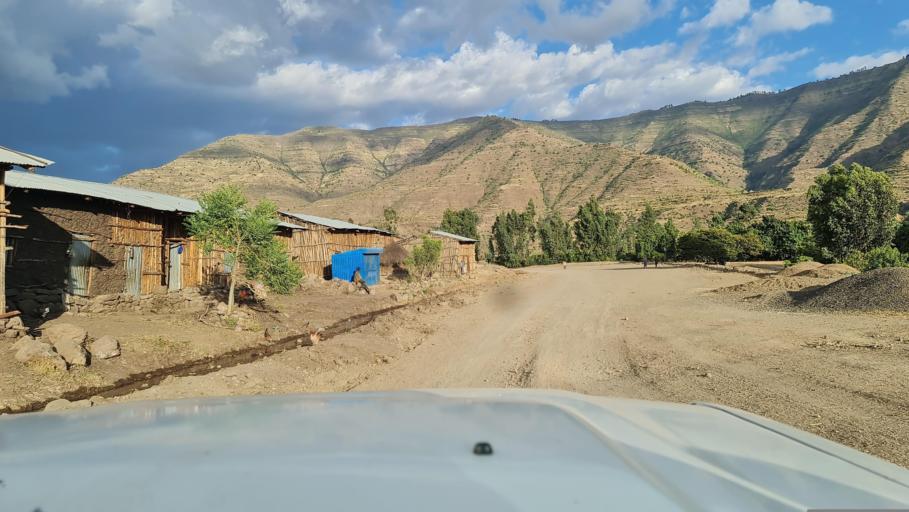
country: ET
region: Amhara
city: Debark'
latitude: 13.0369
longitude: 38.0454
